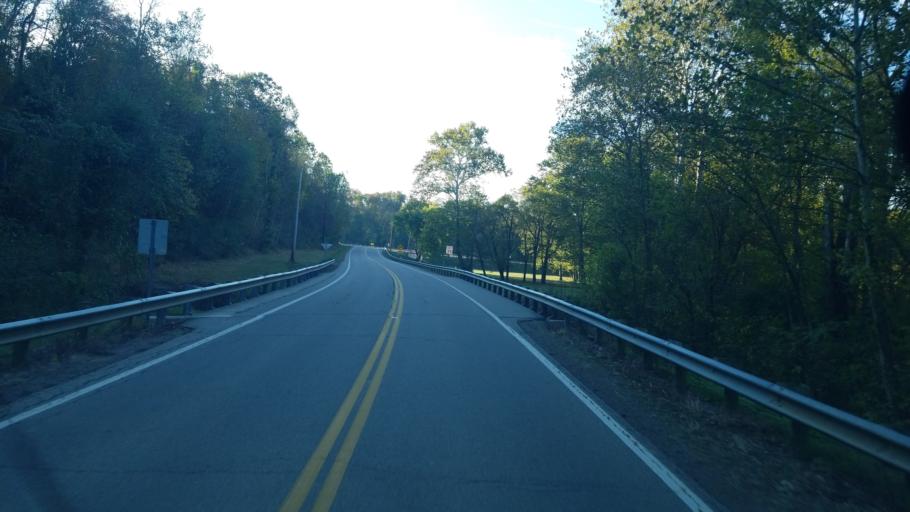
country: US
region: Ohio
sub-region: Jackson County
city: Wellston
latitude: 39.1515
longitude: -82.5170
